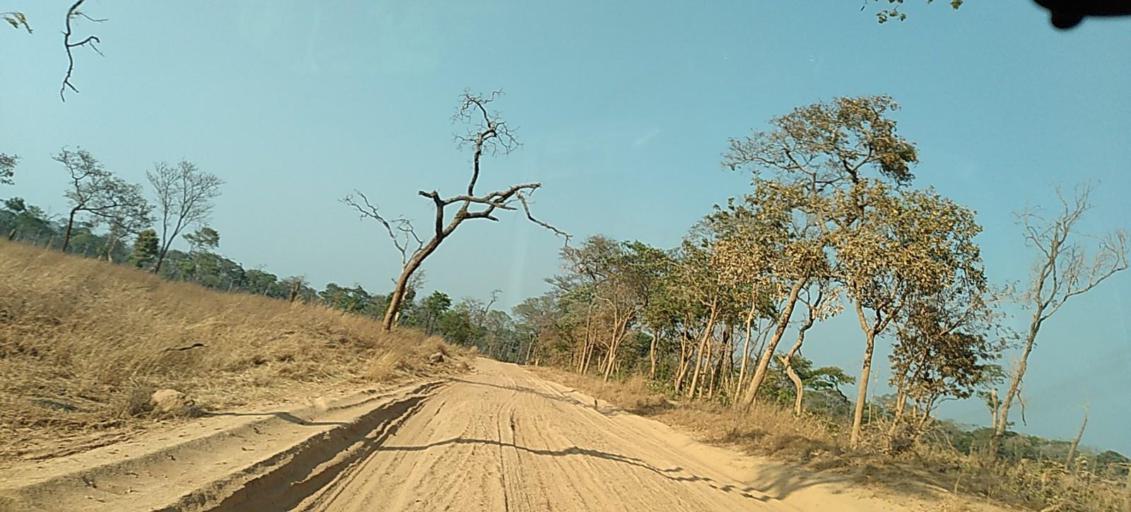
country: ZM
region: North-Western
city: Kasempa
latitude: -13.5706
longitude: 25.9944
